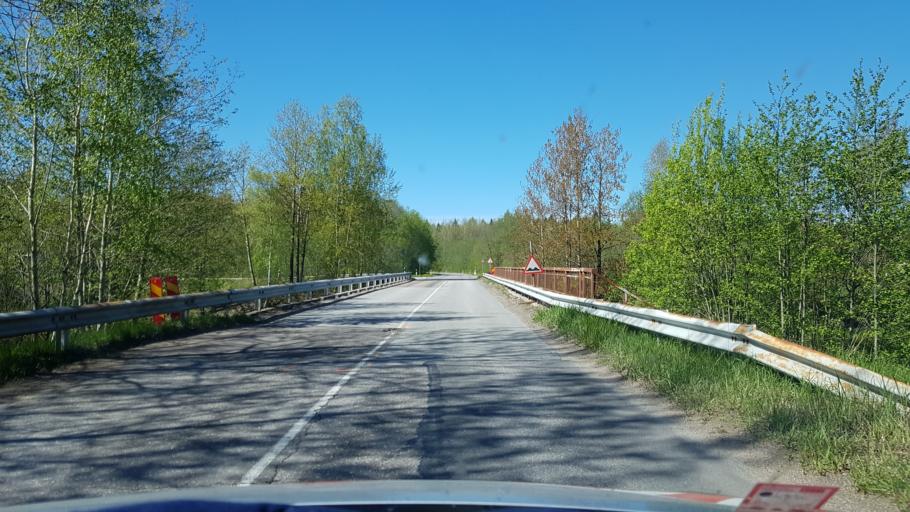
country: EE
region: Ida-Virumaa
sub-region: Narva linn
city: Narva
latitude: 59.3514
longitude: 28.0980
